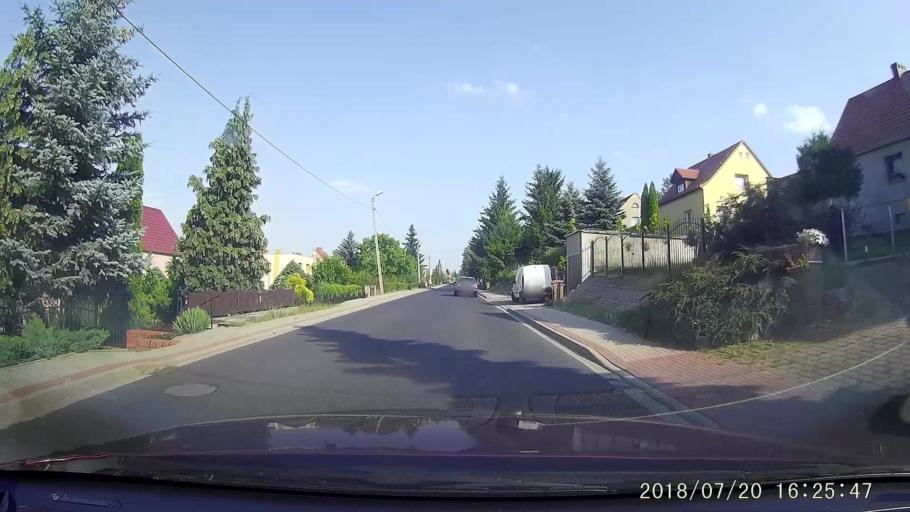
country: PL
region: Lower Silesian Voivodeship
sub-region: Powiat zgorzelecki
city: Lagow
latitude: 51.1326
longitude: 15.0318
